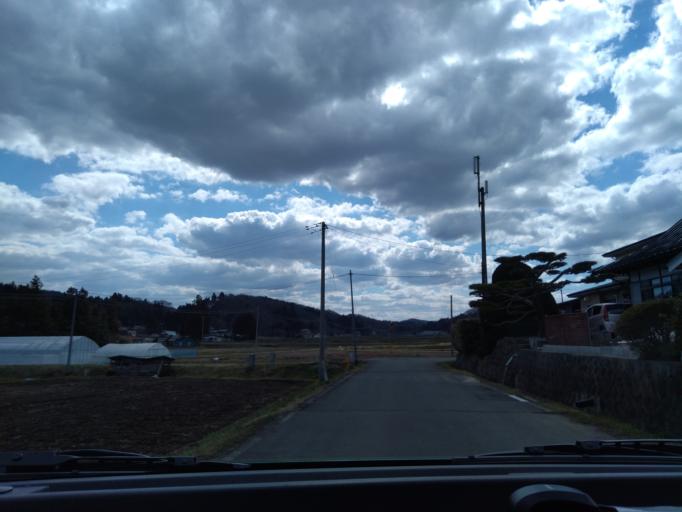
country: JP
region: Iwate
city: Ichinoseki
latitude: 38.9765
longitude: 141.0873
